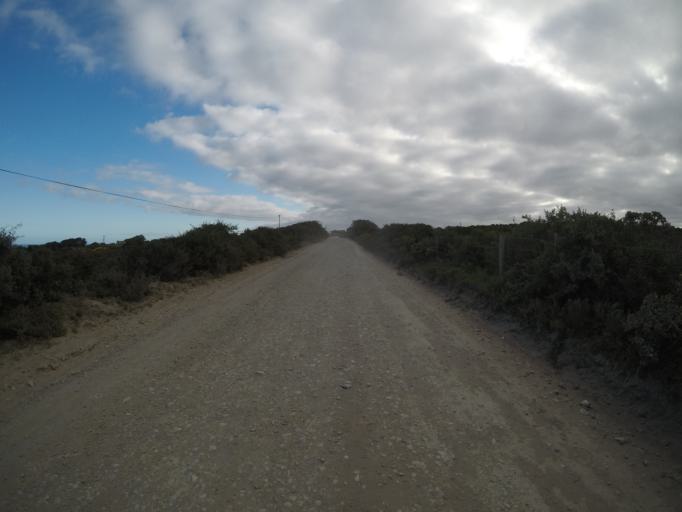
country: ZA
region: Western Cape
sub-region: Eden District Municipality
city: Riversdale
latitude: -34.4178
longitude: 21.3434
